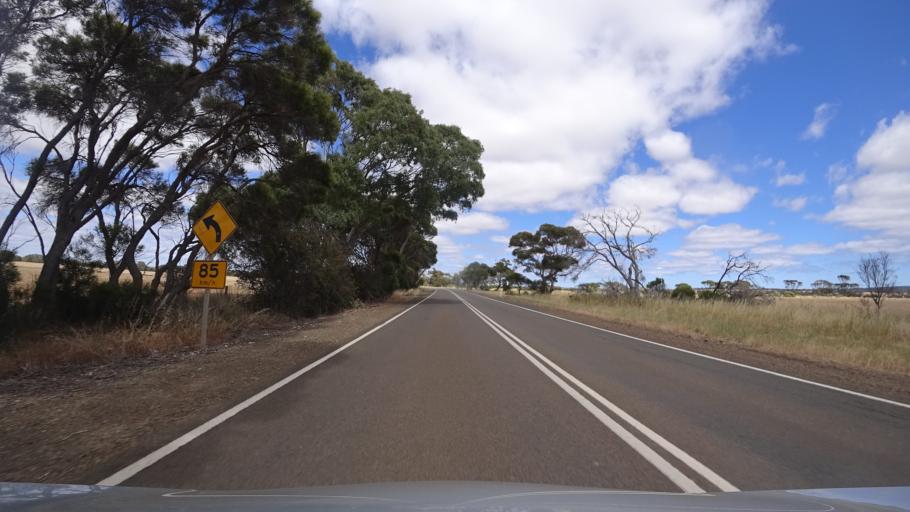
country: AU
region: South Australia
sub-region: Kangaroo Island
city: Kingscote
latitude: -35.6820
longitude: 137.5504
